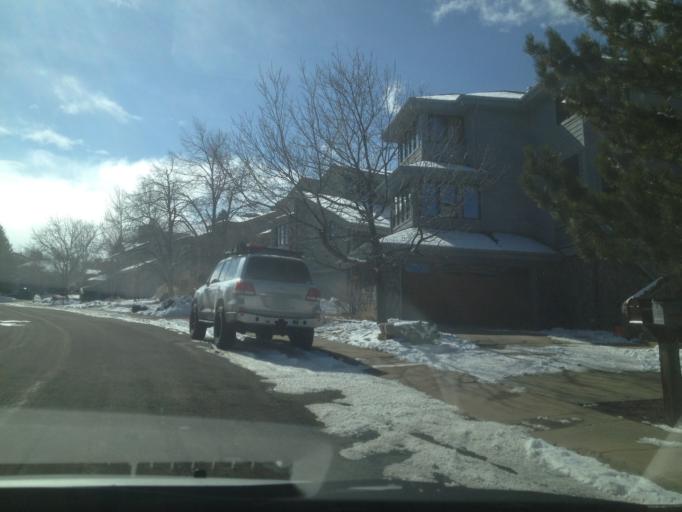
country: US
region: Colorado
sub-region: Boulder County
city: Boulder
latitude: 40.0463
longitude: -105.2938
